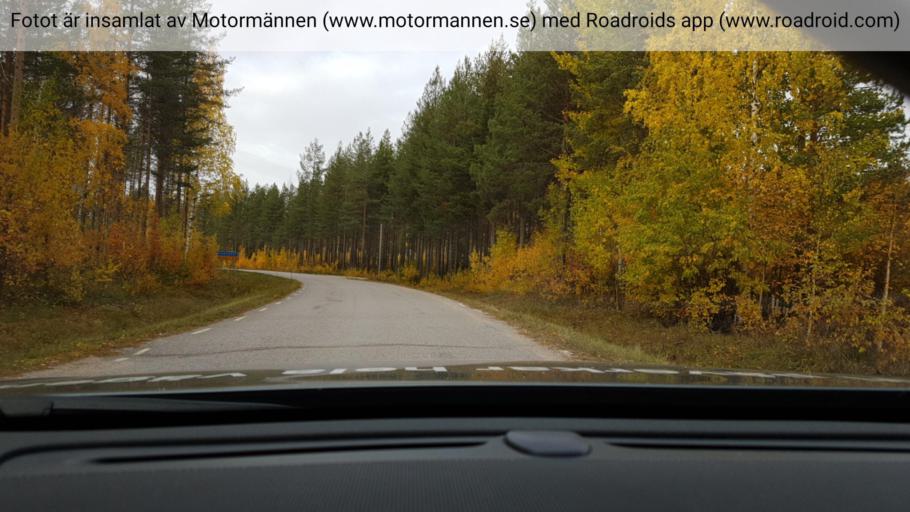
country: SE
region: Norrbotten
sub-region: Overkalix Kommun
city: OEverkalix
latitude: 66.2594
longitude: 23.1095
